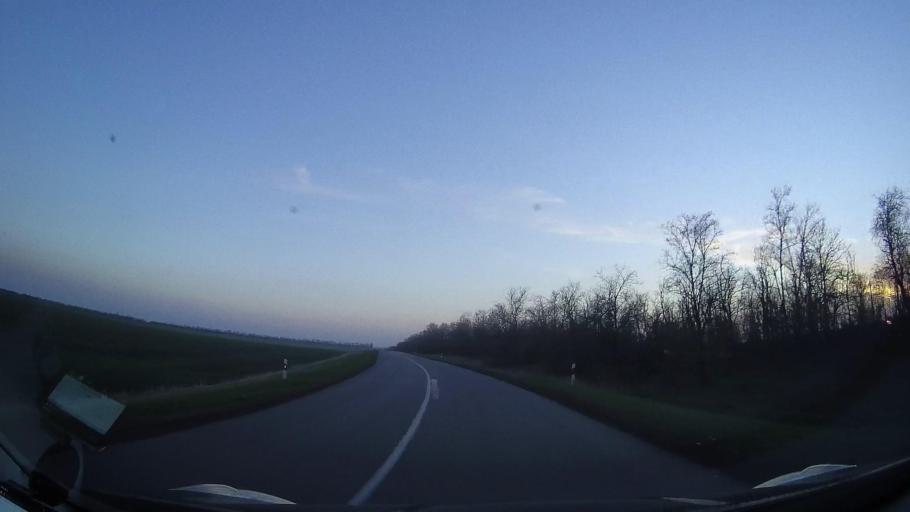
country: RU
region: Rostov
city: Zernograd
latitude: 46.9239
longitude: 40.3388
